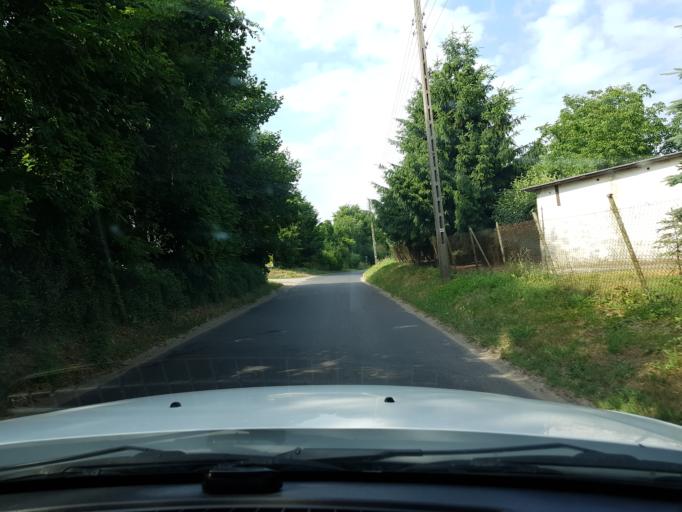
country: PL
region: West Pomeranian Voivodeship
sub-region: Powiat gryfinski
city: Chojna
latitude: 52.9644
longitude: 14.4543
